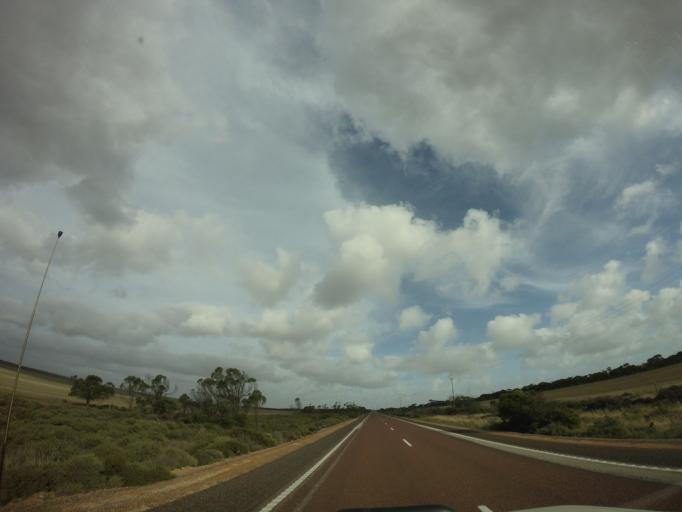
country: AU
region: South Australia
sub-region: Ceduna
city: Ceduna
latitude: -32.0623
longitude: 133.6203
